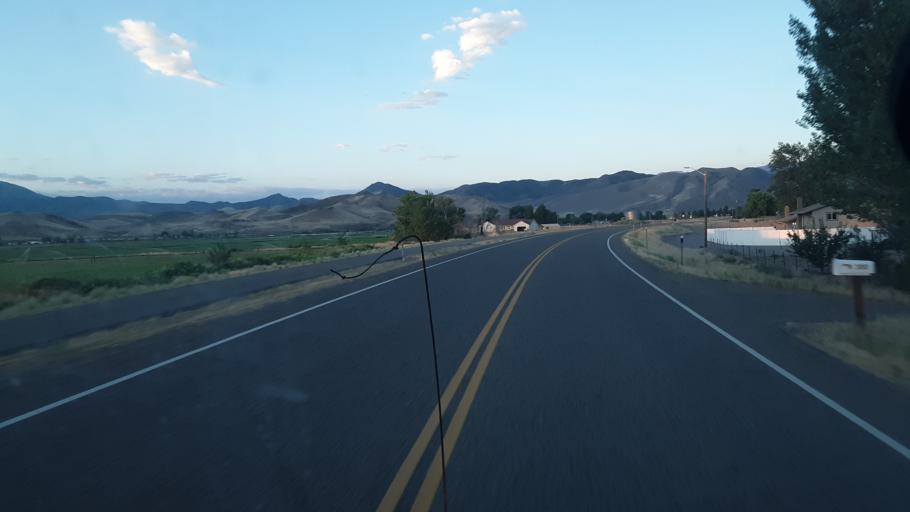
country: US
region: Utah
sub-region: Sevier County
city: Monroe
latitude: 38.6192
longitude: -112.2187
